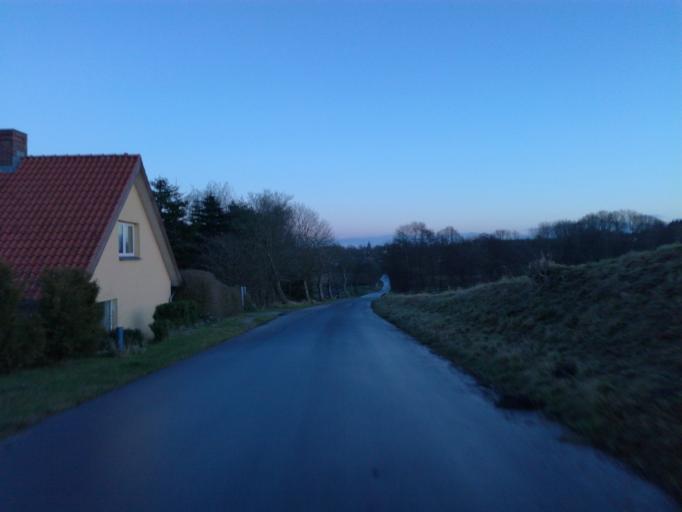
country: DK
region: South Denmark
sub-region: Fredericia Kommune
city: Snoghoj
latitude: 55.5528
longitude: 9.6859
